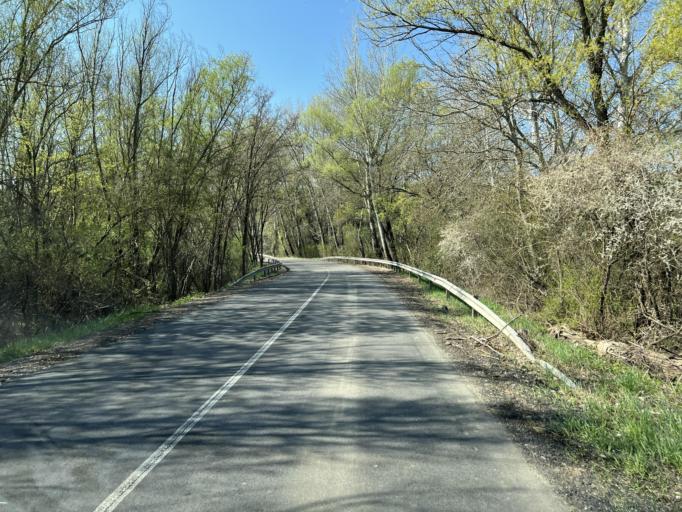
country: HU
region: Pest
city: Orbottyan
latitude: 47.7315
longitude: 19.2696
